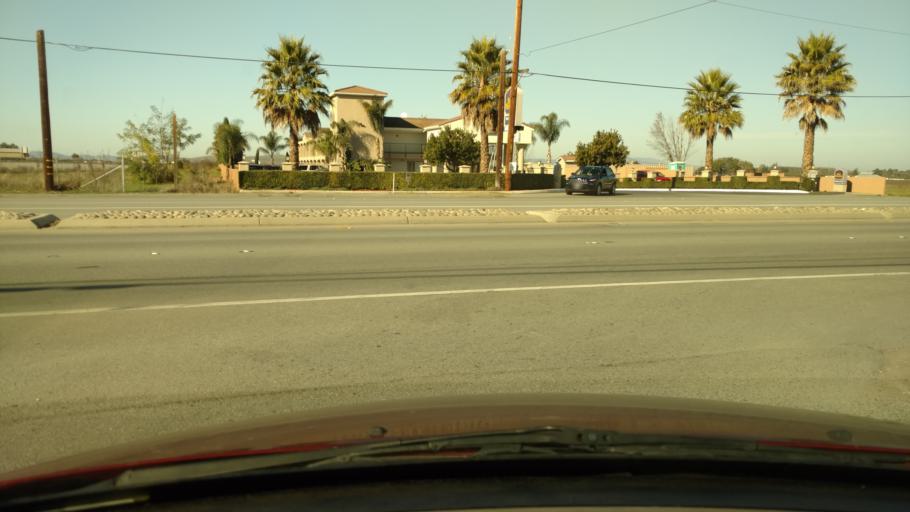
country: US
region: California
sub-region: San Benito County
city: Hollister
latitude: 36.8658
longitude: -121.4011
